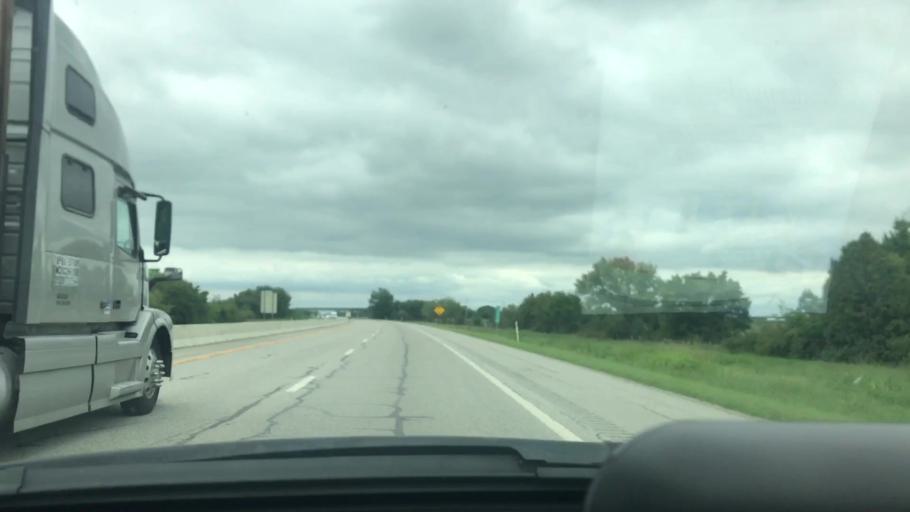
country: US
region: Oklahoma
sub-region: Ottawa County
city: Fairland
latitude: 36.7380
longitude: -94.9096
